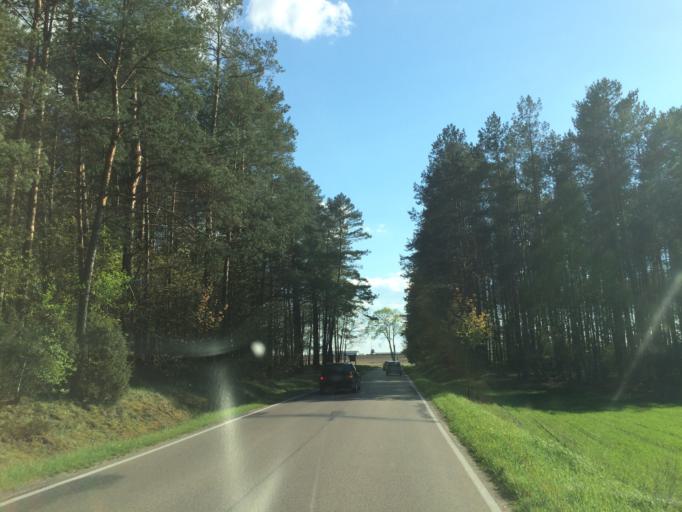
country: PL
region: Warmian-Masurian Voivodeship
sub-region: Powiat dzialdowski
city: Lidzbark
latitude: 53.2798
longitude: 19.8443
